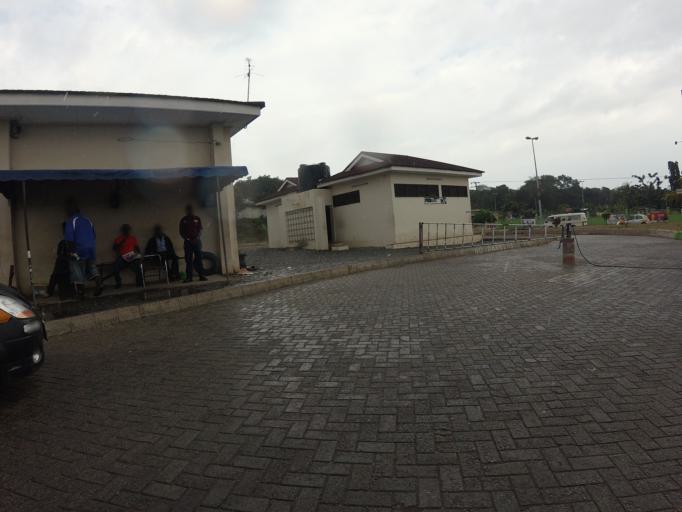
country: GH
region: Greater Accra
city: Dome
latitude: 5.6217
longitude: -0.2254
